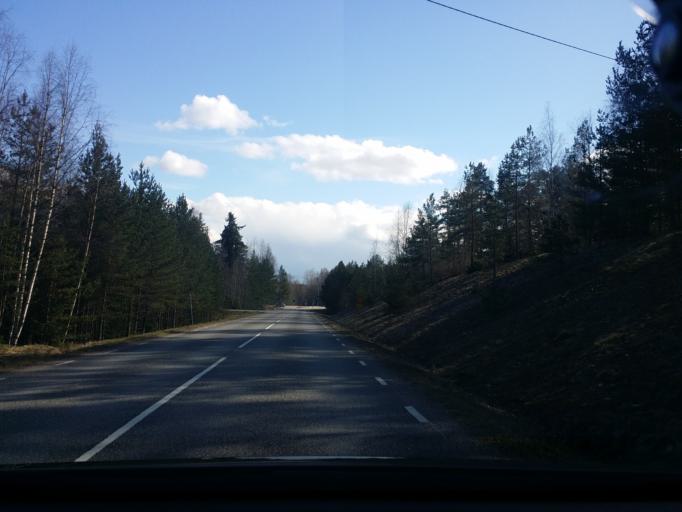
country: SE
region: Vaestmanland
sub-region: Sala Kommun
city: Sala
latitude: 59.9866
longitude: 16.4755
